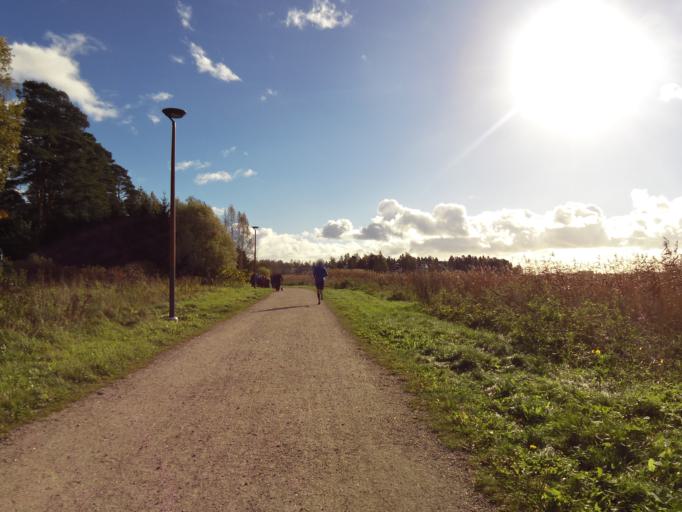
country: FI
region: Uusimaa
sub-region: Helsinki
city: Koukkuniemi
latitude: 60.1498
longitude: 24.7253
